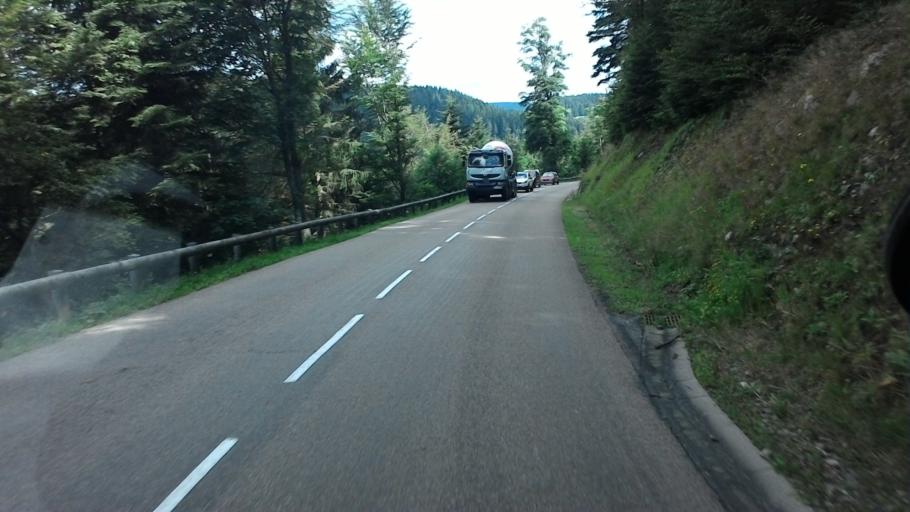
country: FR
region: Lorraine
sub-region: Departement des Vosges
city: La Bresse
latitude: 48.0361
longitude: 6.8624
